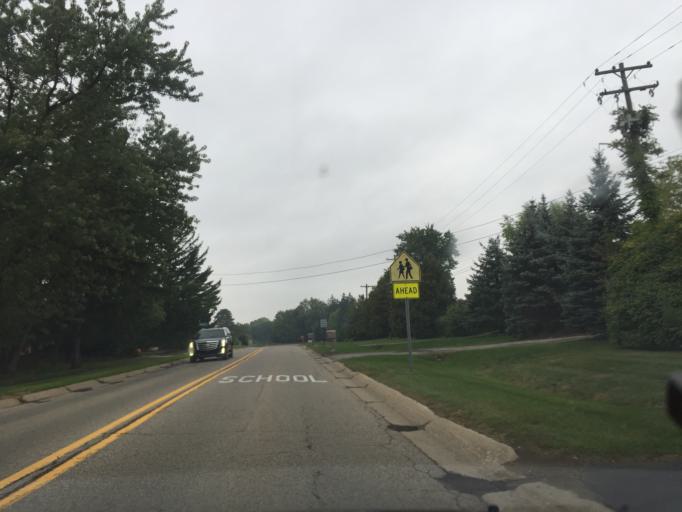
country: US
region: Michigan
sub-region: Oakland County
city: Orchard Lake
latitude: 42.5695
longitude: -83.3305
